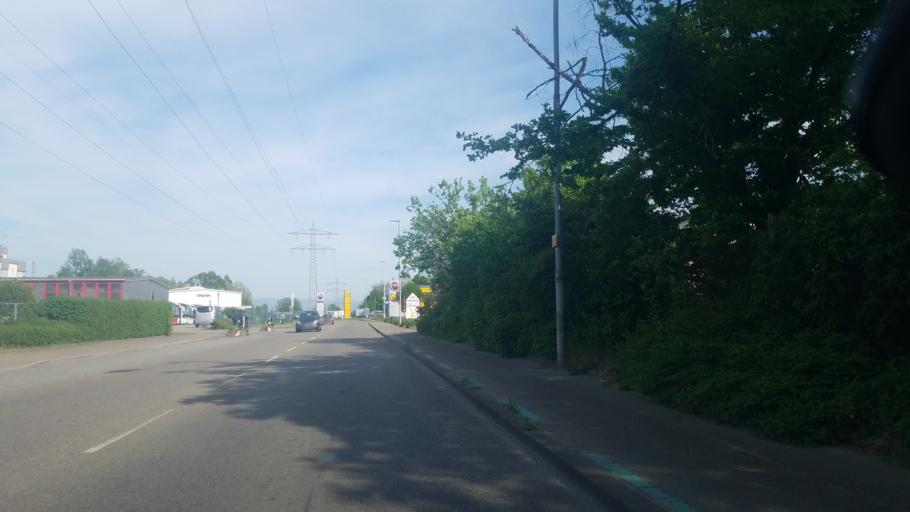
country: DE
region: Baden-Wuerttemberg
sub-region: Freiburg Region
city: Kehl
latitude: 48.5510
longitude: 7.8396
